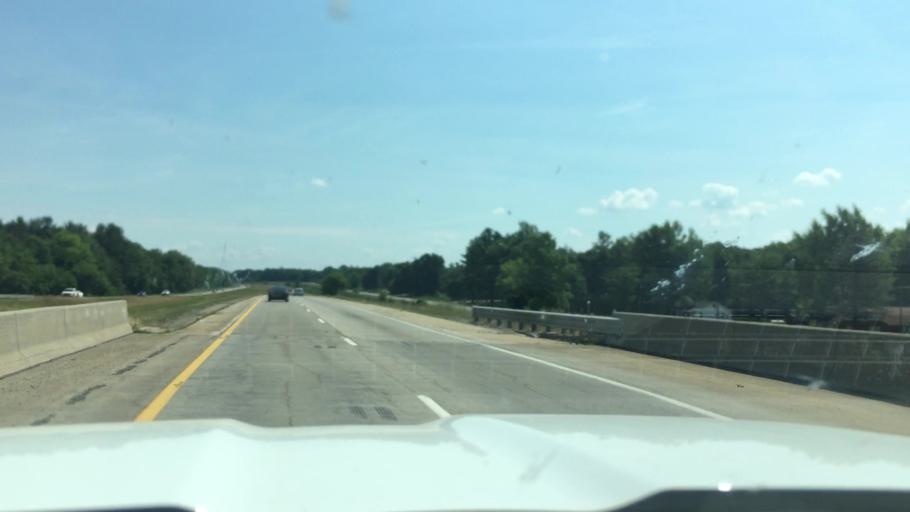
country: US
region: Michigan
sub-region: Shiawassee County
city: Perry
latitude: 42.8133
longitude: -84.2935
